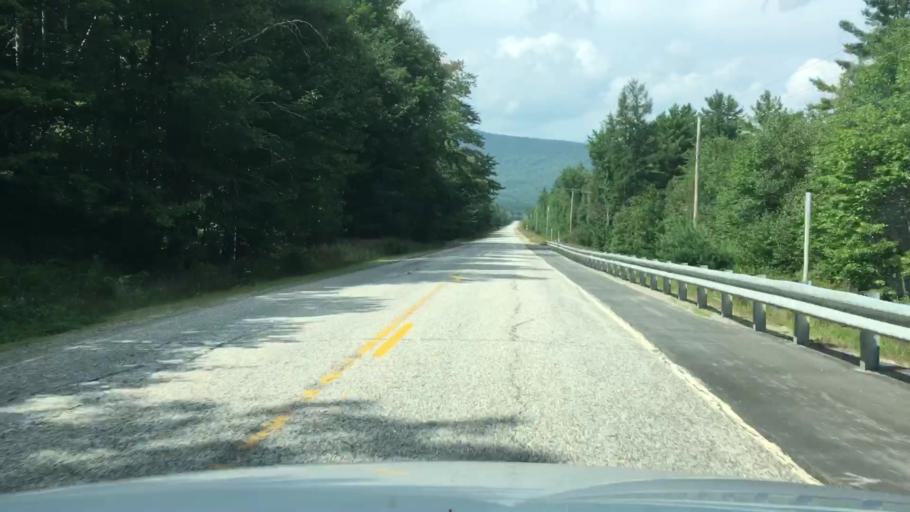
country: US
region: Maine
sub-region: Oxford County
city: Rumford
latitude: 44.5698
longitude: -70.7185
